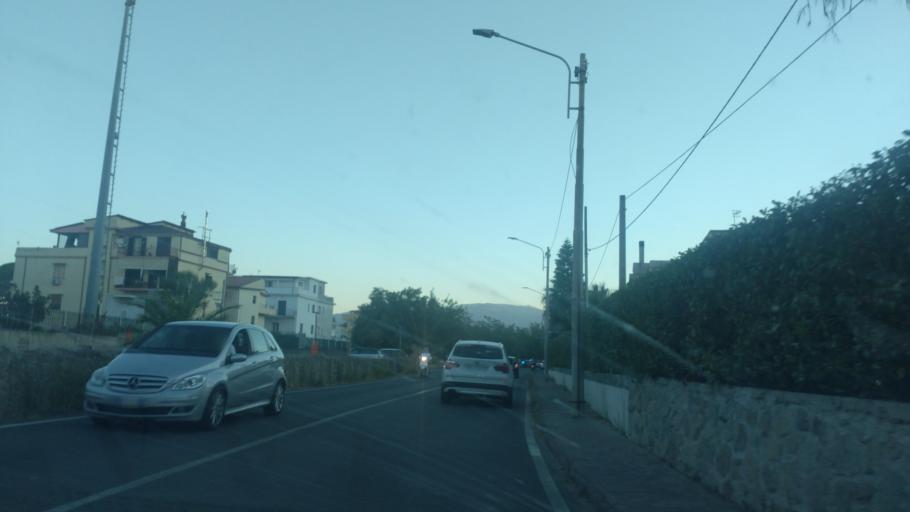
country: IT
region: Calabria
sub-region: Provincia di Catanzaro
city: Montepaone Lido
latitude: 38.7309
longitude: 16.5439
